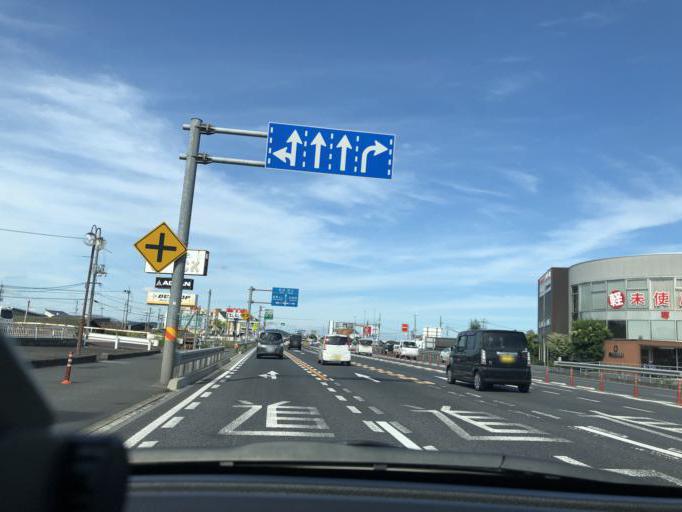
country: JP
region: Okayama
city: Kurashiki
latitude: 34.5891
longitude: 133.7949
